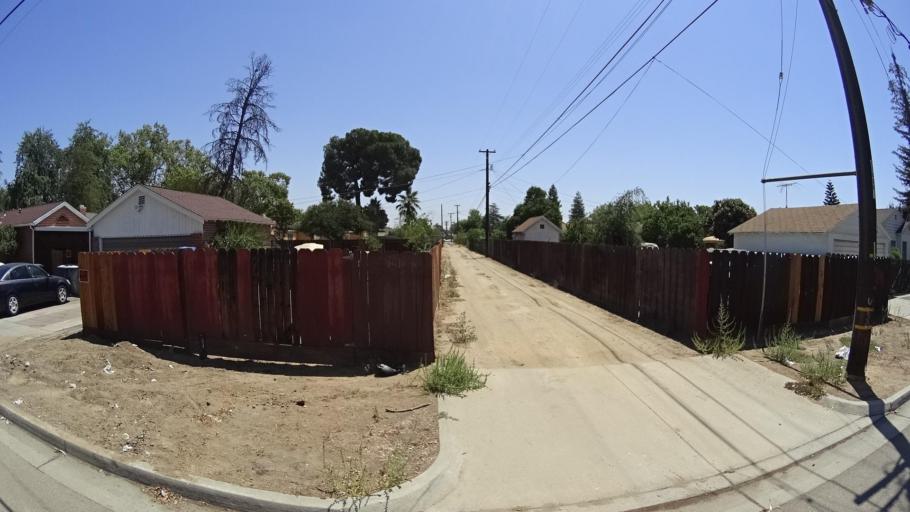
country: US
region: California
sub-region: Fresno County
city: Fresno
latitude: 36.7673
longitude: -119.7747
